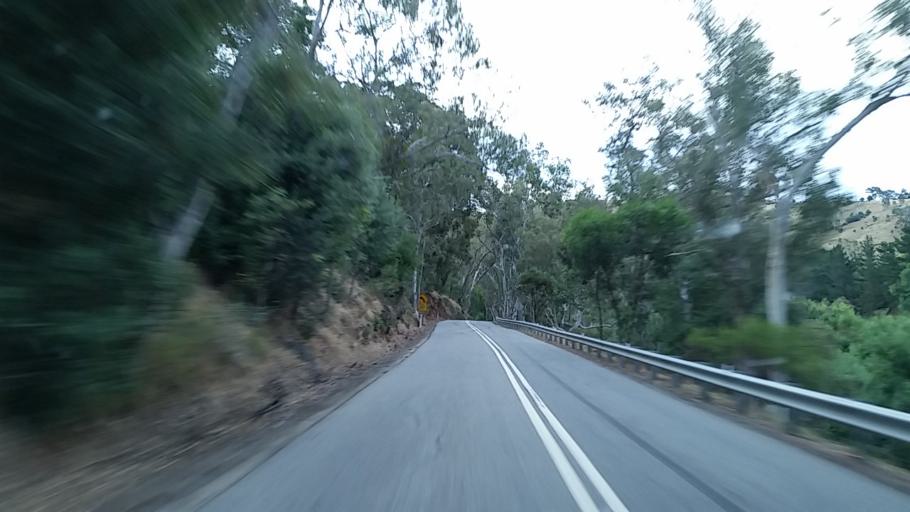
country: AU
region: South Australia
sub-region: Campbelltown
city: Athelstone
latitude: -34.8662
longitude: 138.7576
